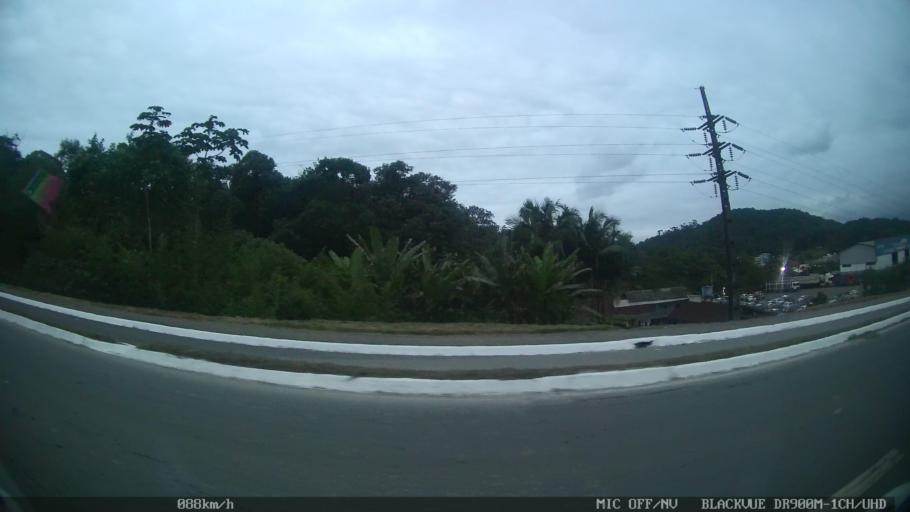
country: BR
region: Santa Catarina
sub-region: Joinville
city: Joinville
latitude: -26.3117
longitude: -48.8760
